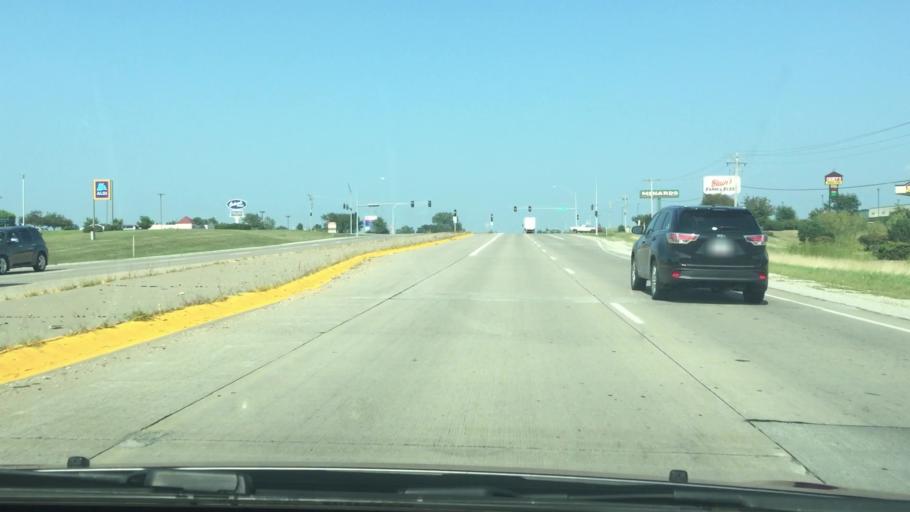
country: US
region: Iowa
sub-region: Muscatine County
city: Muscatine
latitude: 41.4583
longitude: -91.0196
